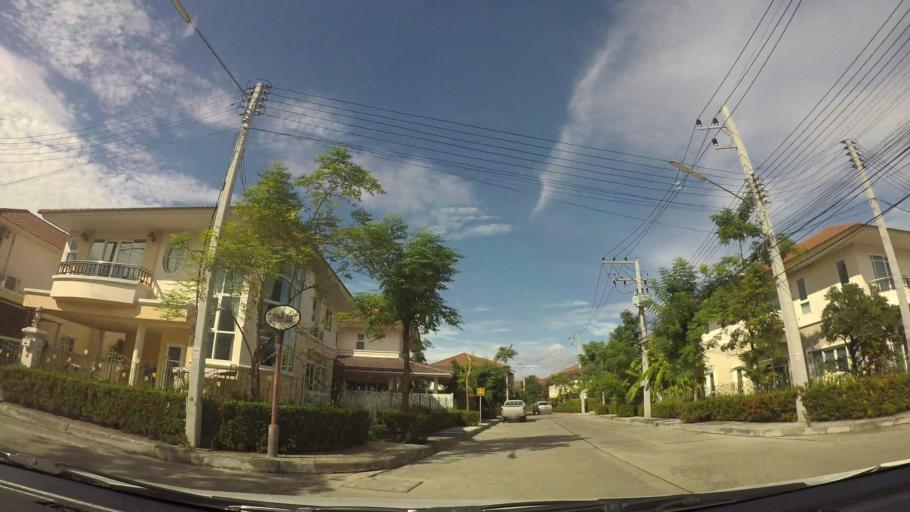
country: TH
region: Chiang Mai
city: Saraphi
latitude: 18.7579
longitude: 99.0348
